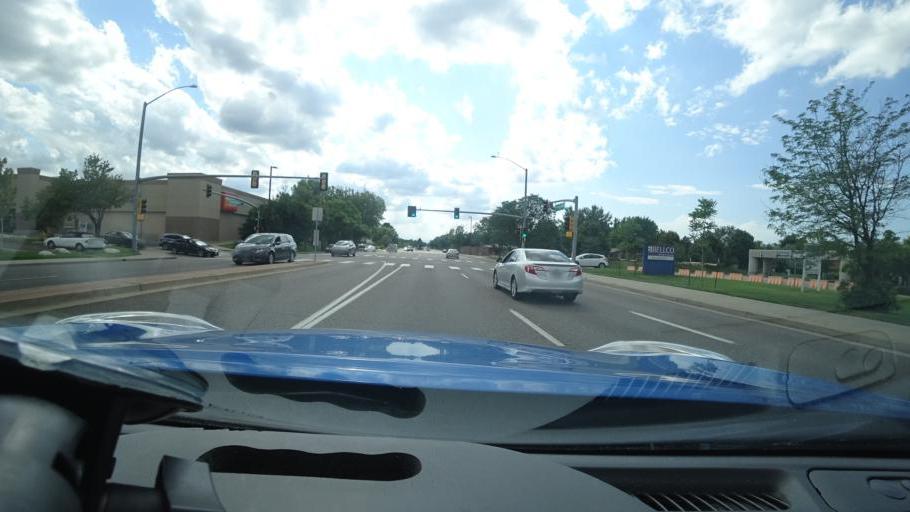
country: US
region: Colorado
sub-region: Adams County
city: Aurora
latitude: 39.6966
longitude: -104.8671
